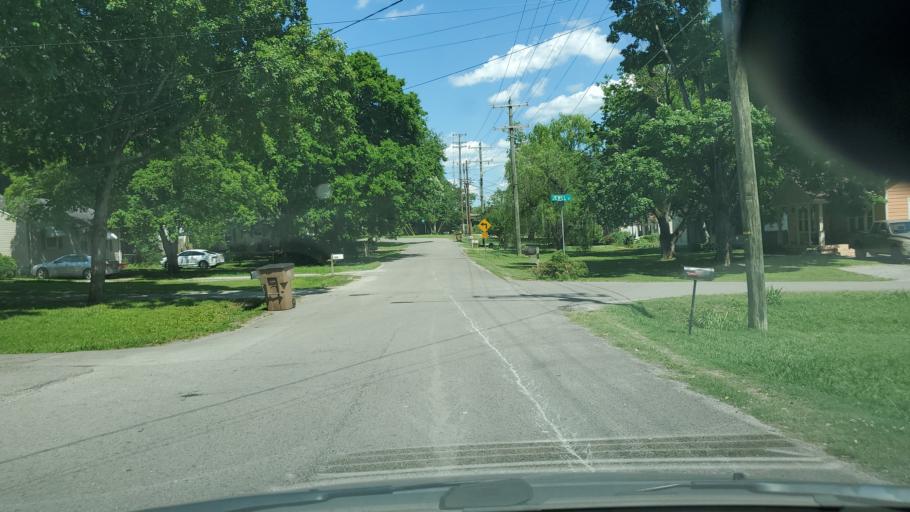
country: US
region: Tennessee
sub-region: Davidson County
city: Nashville
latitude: 36.1957
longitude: -86.7546
